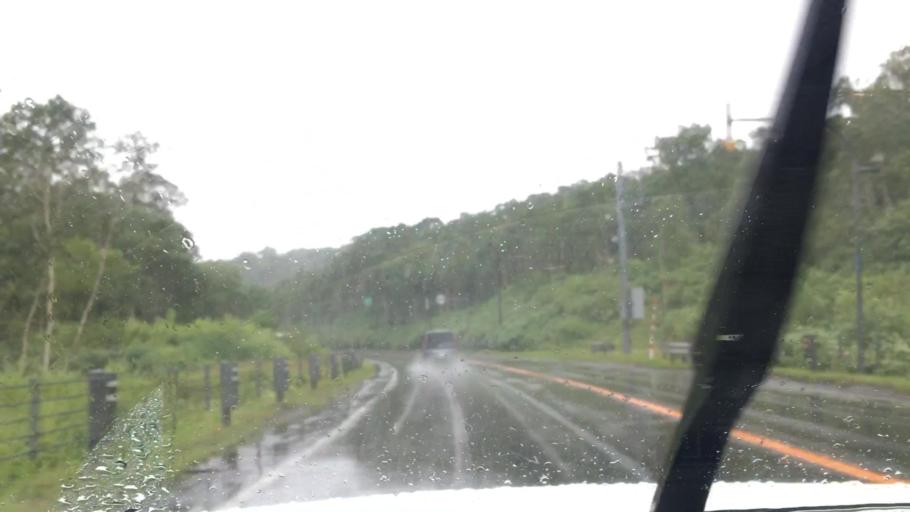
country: JP
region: Hokkaido
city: Sapporo
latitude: 42.8634
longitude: 141.1054
